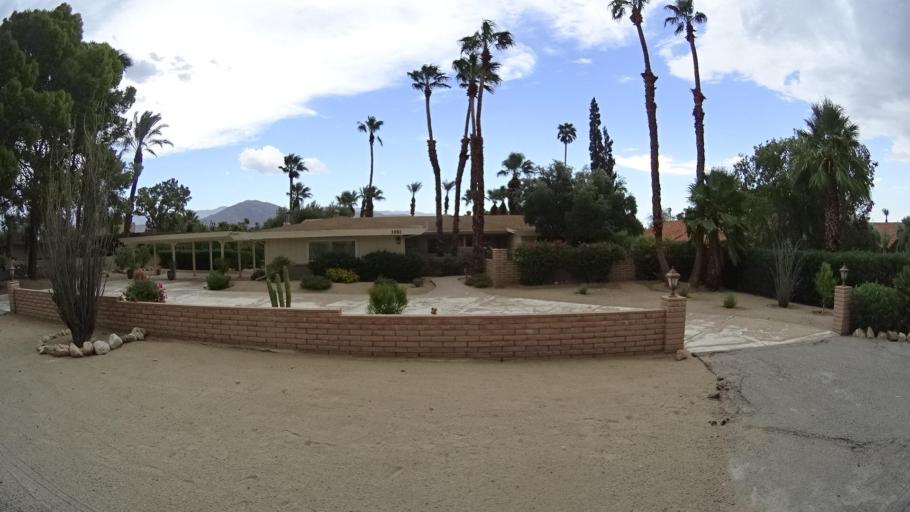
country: US
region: California
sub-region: San Diego County
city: Borrego Springs
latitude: 33.2927
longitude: -116.3905
